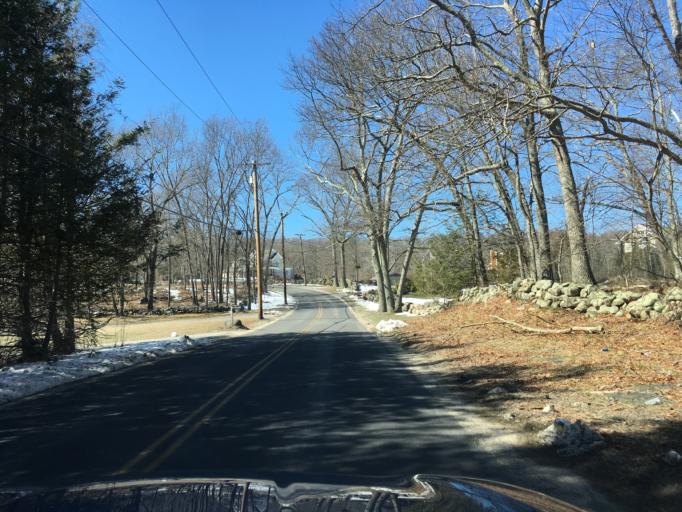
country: US
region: Rhode Island
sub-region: Washington County
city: Exeter
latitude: 41.6078
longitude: -71.5053
